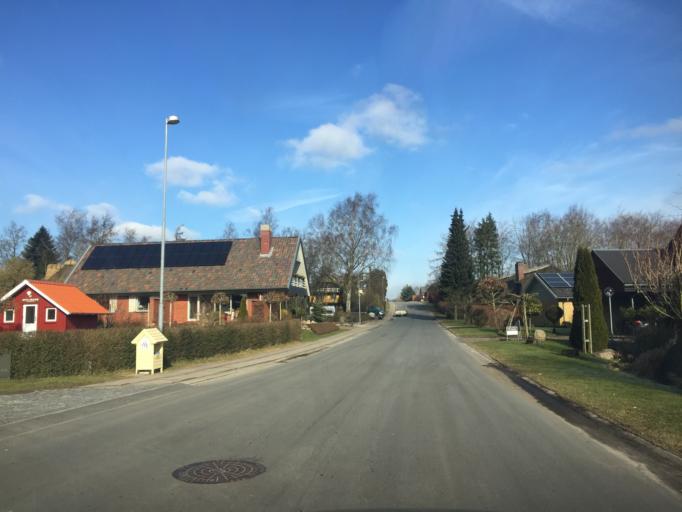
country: DK
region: South Denmark
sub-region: Nordfyns Kommune
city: Sonderso
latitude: 55.4464
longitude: 10.1923
